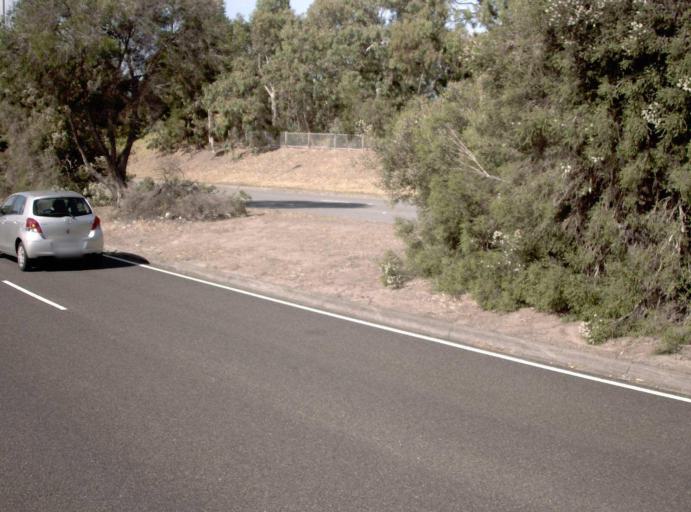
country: AU
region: Victoria
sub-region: Kingston
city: Mordialloc
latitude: -38.0001
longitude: 145.0842
